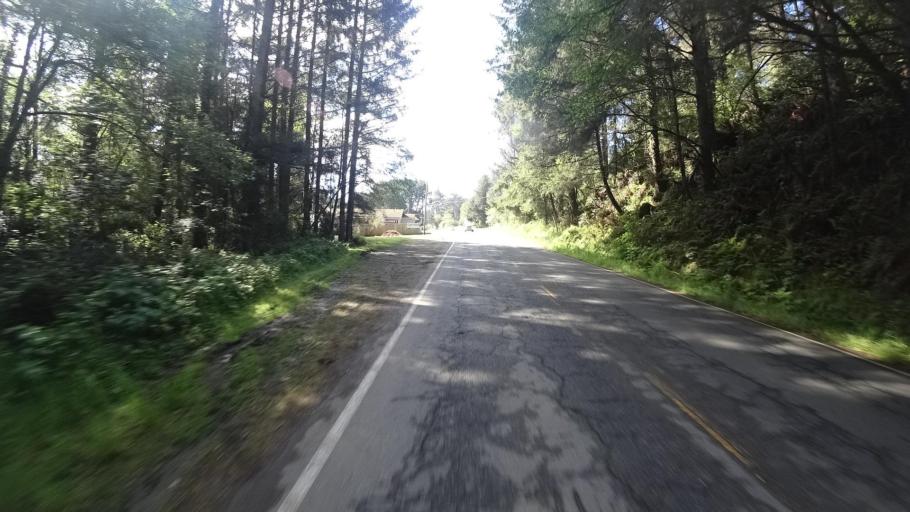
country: US
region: California
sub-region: Humboldt County
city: McKinleyville
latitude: 40.9901
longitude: -124.1104
